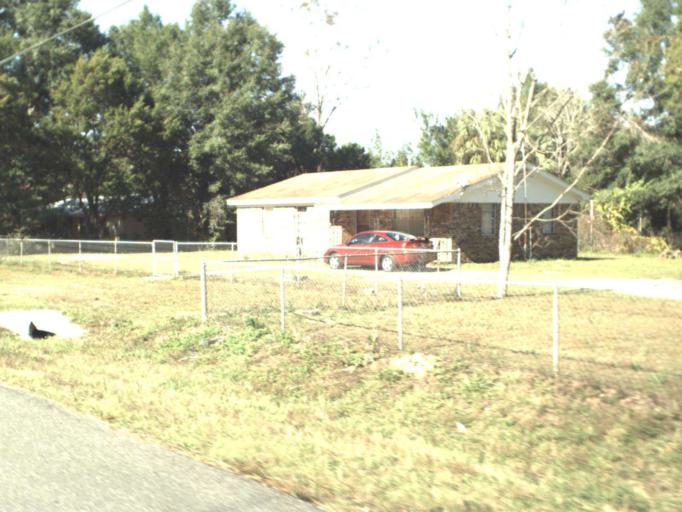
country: US
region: Florida
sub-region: Okaloosa County
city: Crestview
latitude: 30.7602
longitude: -86.6580
